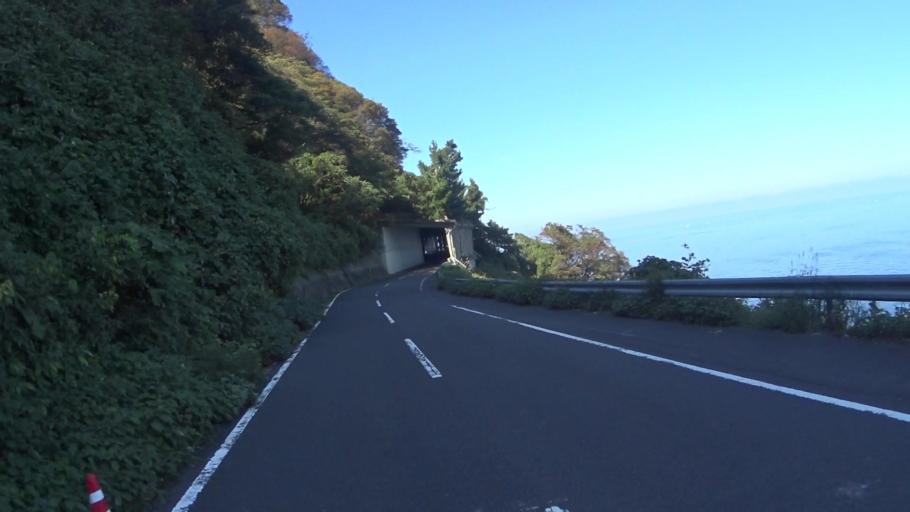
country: JP
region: Kyoto
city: Miyazu
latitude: 35.7610
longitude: 135.2404
